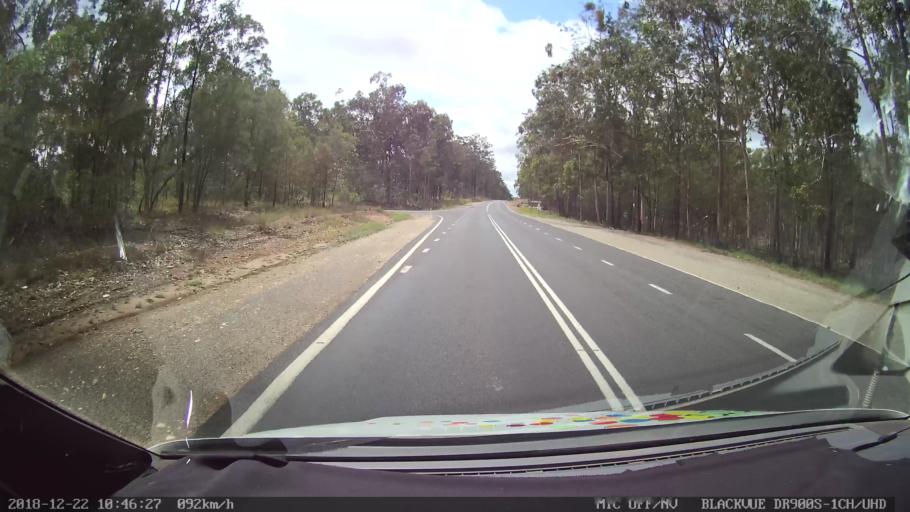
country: AU
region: New South Wales
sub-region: Clarence Valley
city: South Grafton
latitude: -29.6660
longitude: 152.8256
